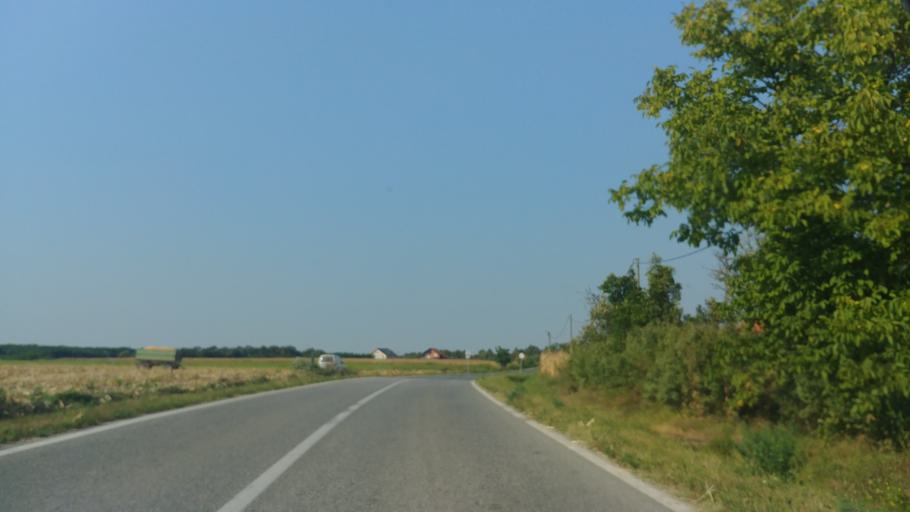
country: BA
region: Brcko
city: Brcko
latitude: 44.7785
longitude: 18.8103
